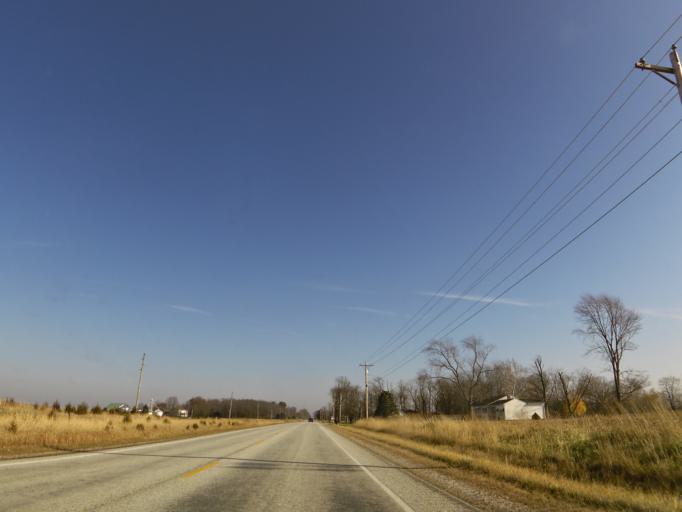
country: US
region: Indiana
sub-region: Shelby County
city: Shelbyville
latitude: 39.5416
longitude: -85.7002
